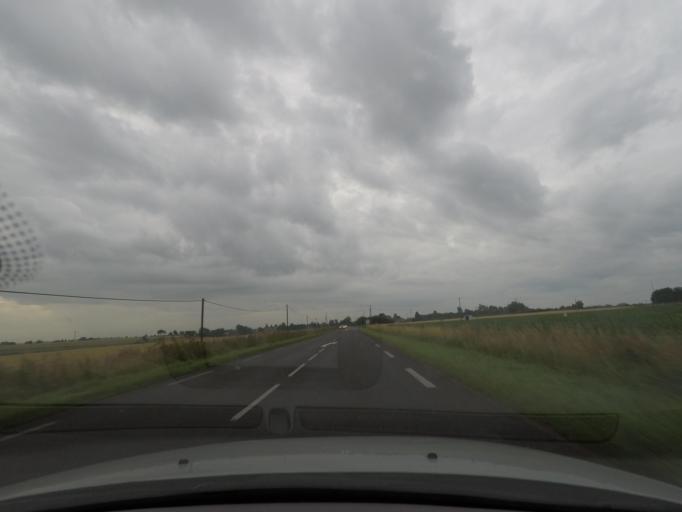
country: FR
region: Haute-Normandie
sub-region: Departement de la Seine-Maritime
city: Neufchatel-en-Bray
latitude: 49.7346
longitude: 1.5017
